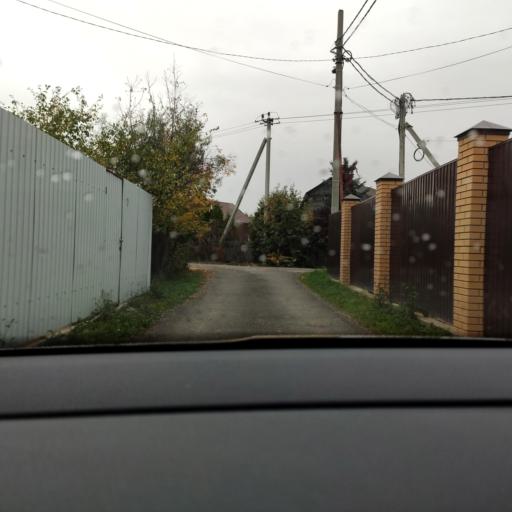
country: RU
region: Moskovskaya
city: Zagoryanskiy
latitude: 55.9646
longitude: 37.9652
